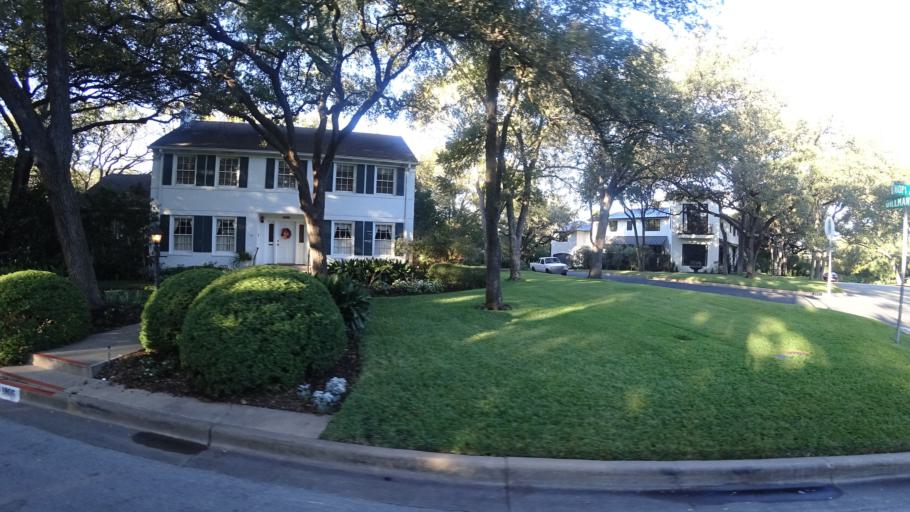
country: US
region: Texas
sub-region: Travis County
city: Rollingwood
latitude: 30.2963
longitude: -97.7733
